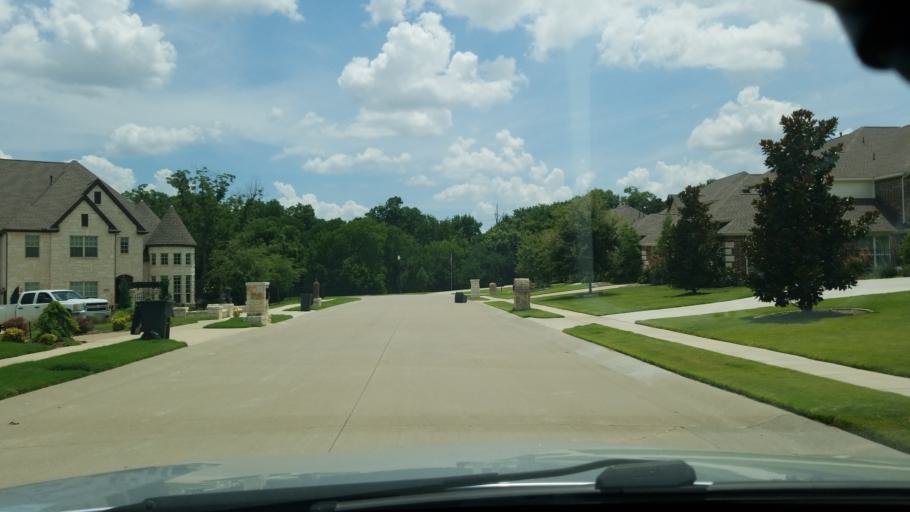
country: US
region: Texas
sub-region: Dallas County
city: Coppell
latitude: 32.9561
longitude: -96.9812
